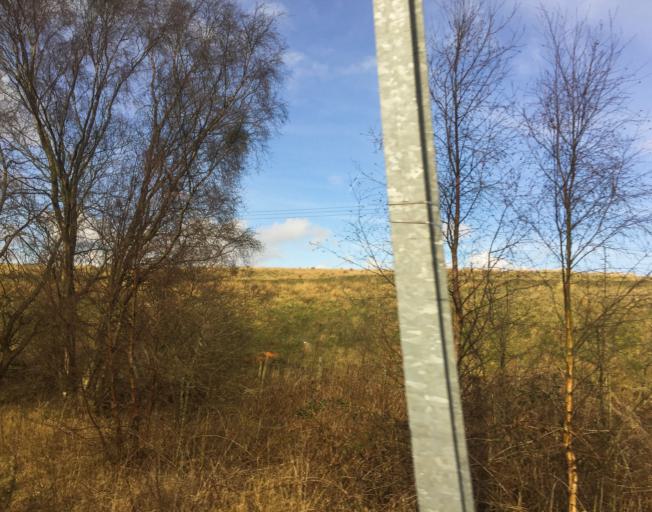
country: GB
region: Scotland
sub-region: North Lanarkshire
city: Glenboig
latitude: 55.8800
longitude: -4.0512
